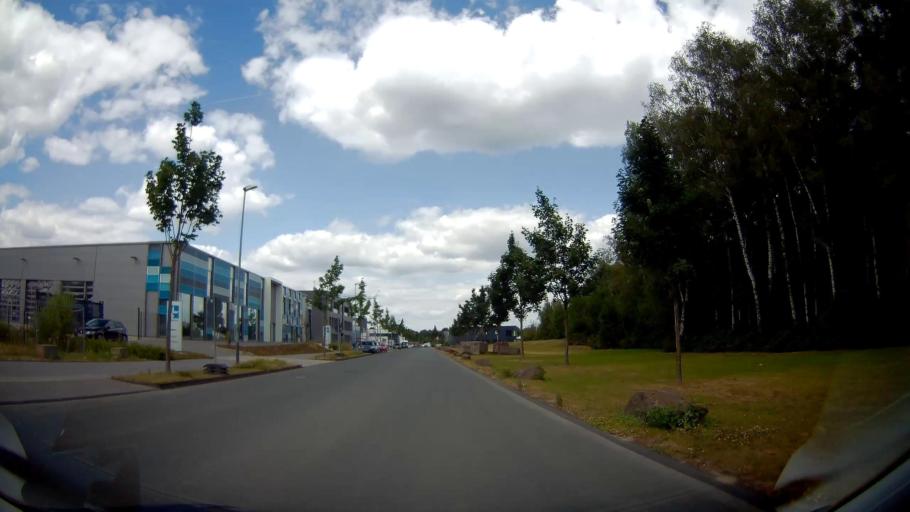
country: DE
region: North Rhine-Westphalia
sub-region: Regierungsbezirk Munster
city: Gelsenkirchen
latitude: 51.5403
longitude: 7.0908
